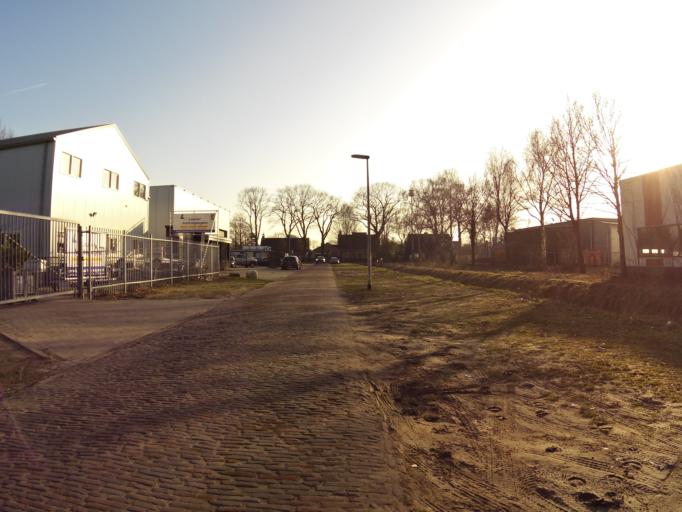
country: NL
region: North Brabant
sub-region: Gemeente Heusden
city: Heusden
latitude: 51.6938
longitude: 5.1603
